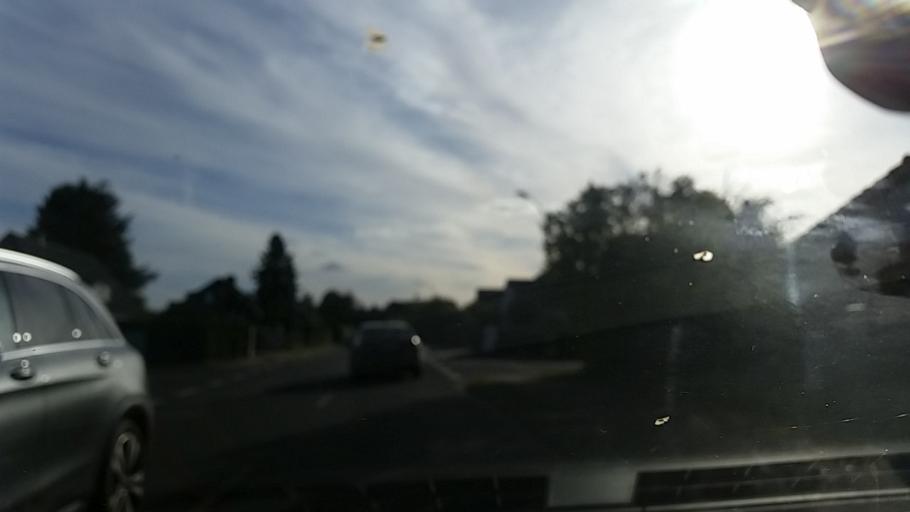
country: DE
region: Schleswig-Holstein
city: Kayhude
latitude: 53.7351
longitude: 10.1526
